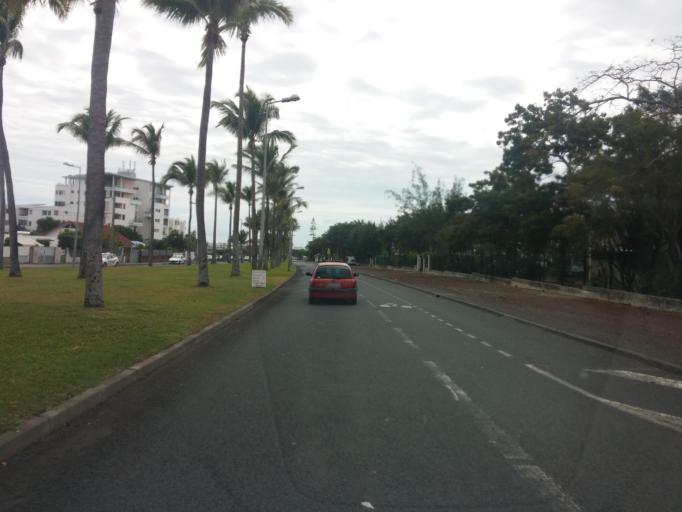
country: RE
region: Reunion
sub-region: Reunion
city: Le Port
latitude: -20.9472
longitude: 55.2935
